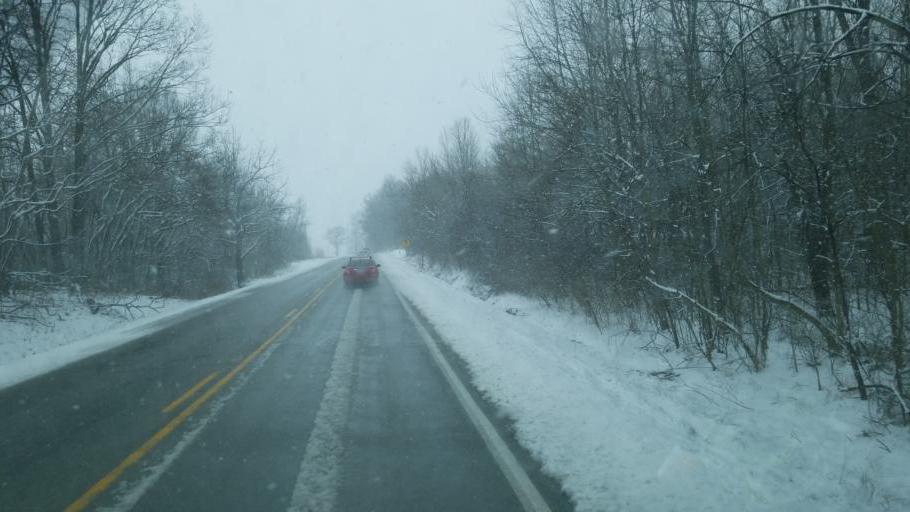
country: US
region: Indiana
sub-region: Wayne County
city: Hagerstown
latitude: 40.0083
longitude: -85.1673
